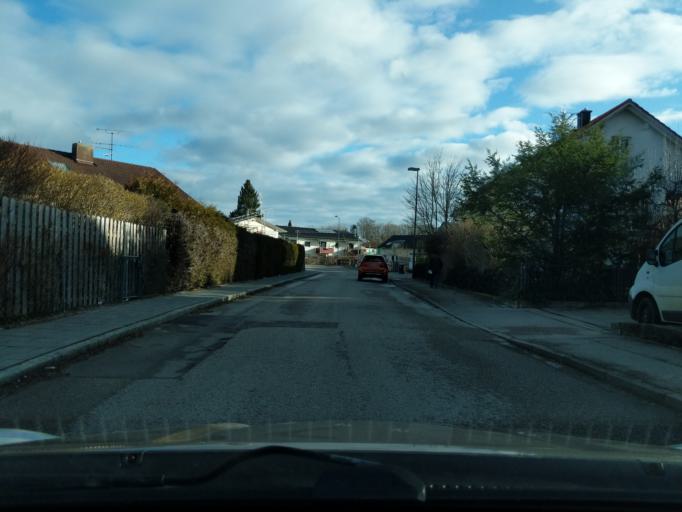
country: DE
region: Bavaria
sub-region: Upper Bavaria
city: Zorneding
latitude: 48.0880
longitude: 11.8275
